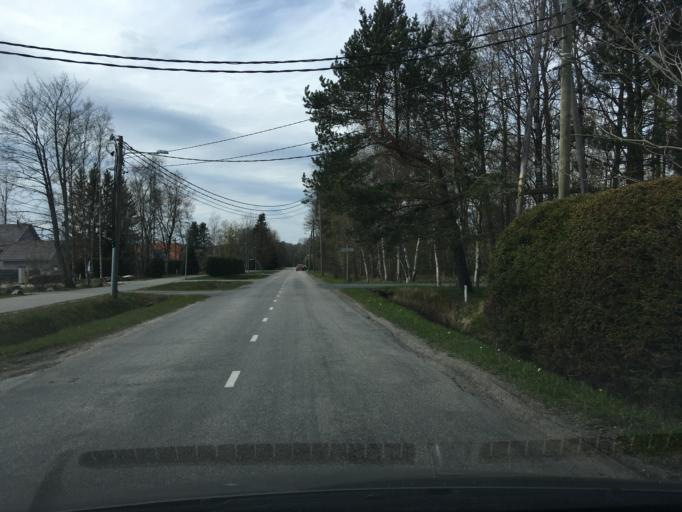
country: EE
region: Harju
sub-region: Joelaehtme vald
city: Loo
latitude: 59.4753
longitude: 24.9268
